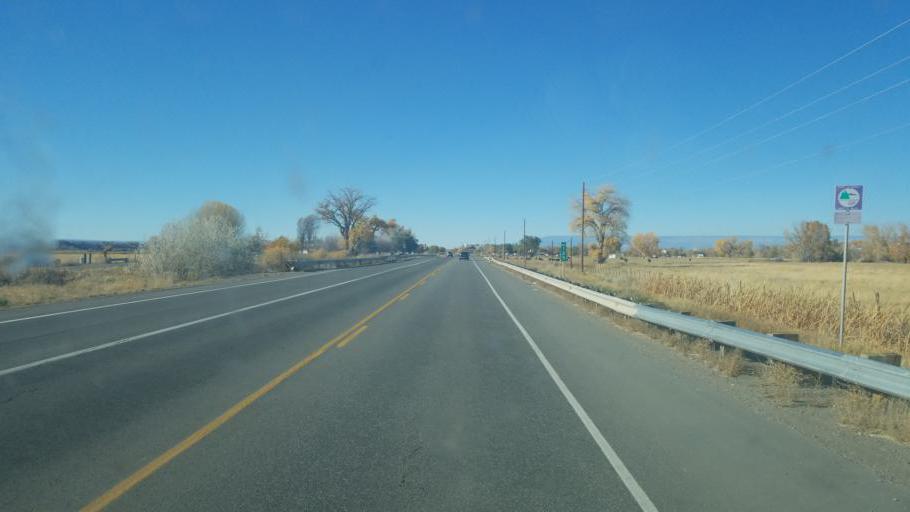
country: US
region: Colorado
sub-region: Montrose County
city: Montrose
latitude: 38.4219
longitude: -107.8567
